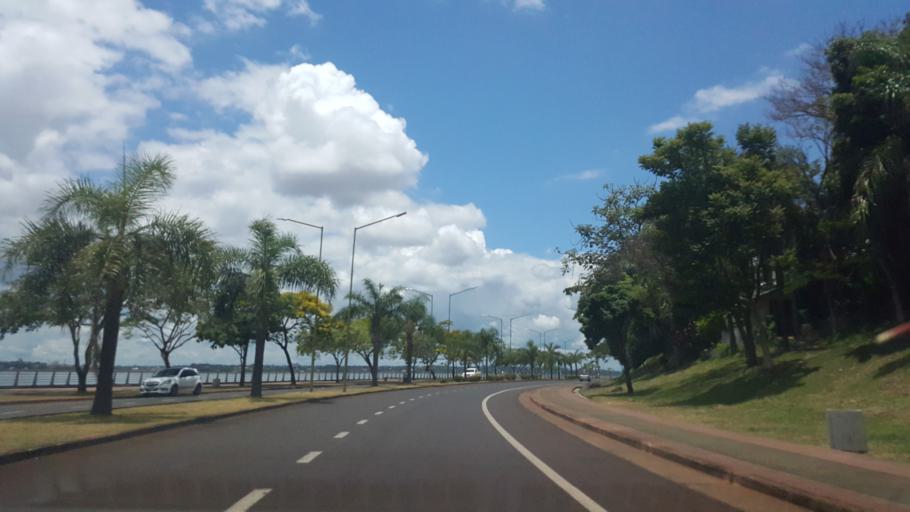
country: AR
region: Misiones
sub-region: Departamento de Capital
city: Posadas
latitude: -27.3522
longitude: -55.8958
